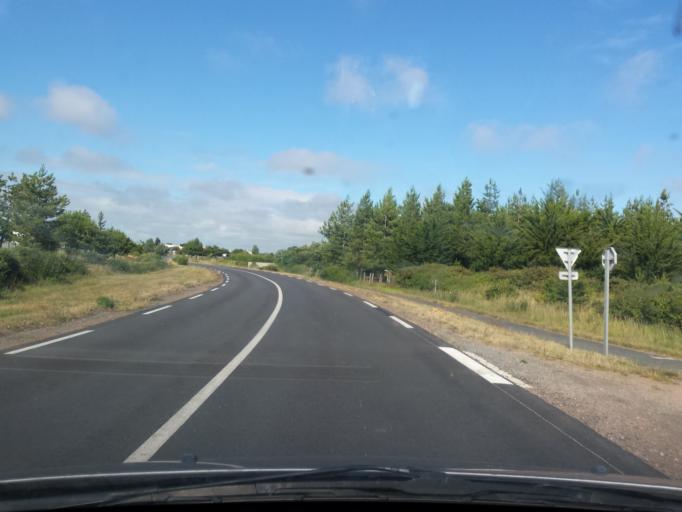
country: FR
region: Pays de la Loire
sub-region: Departement de la Vendee
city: Bretignolles-sur-Mer
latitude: 46.6319
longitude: -1.8401
